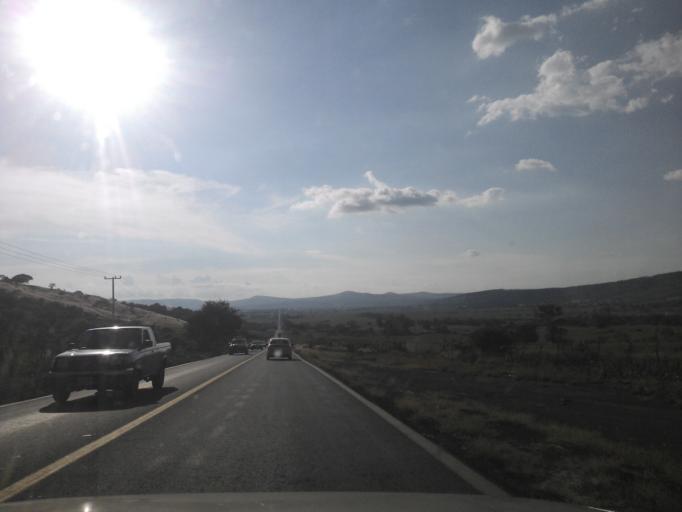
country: MX
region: Jalisco
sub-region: Tototlan
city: Nuevo Refugio de Afuera (Nuevo Refugio)
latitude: 20.5479
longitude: -102.6544
